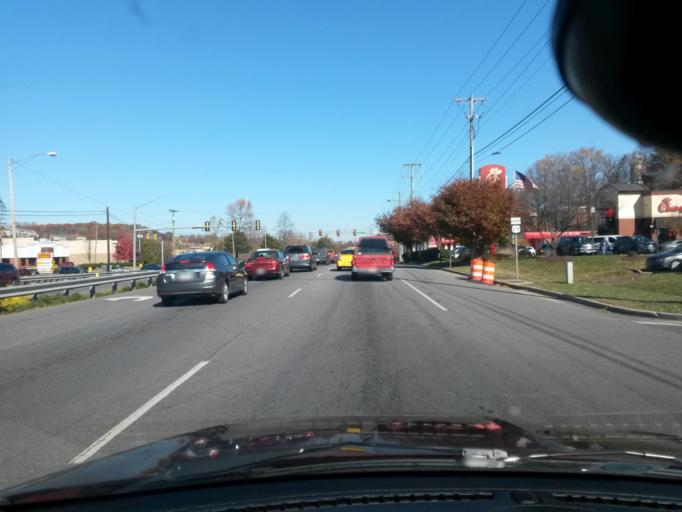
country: US
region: Virginia
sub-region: City of Lynchburg
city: West Lynchburg
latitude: 37.3483
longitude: -79.1862
